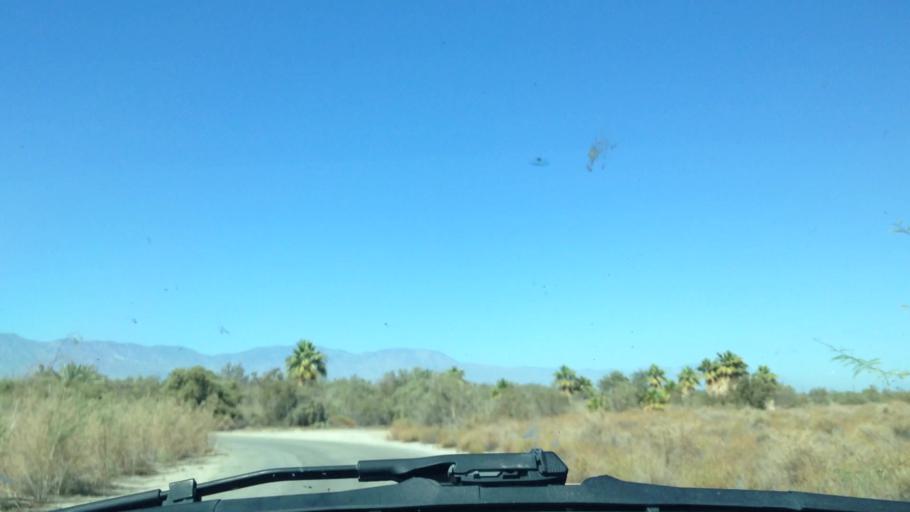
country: US
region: California
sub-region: Imperial County
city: Desert Shores
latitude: 33.5092
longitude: -115.9201
